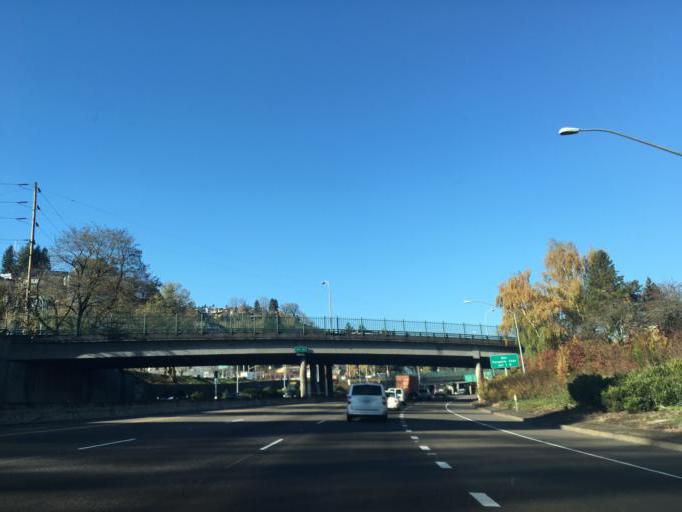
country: US
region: Oregon
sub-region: Multnomah County
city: Portland
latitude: 45.5059
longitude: -122.6808
